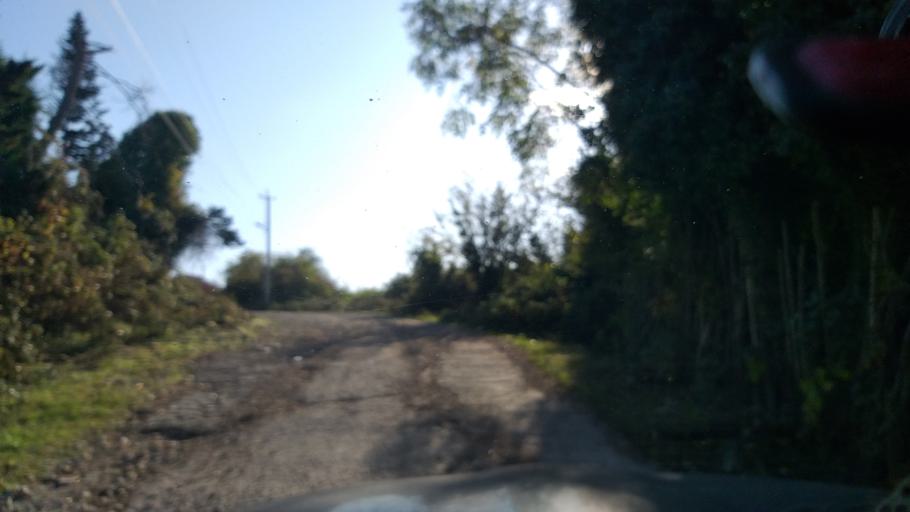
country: GE
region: Abkhazia
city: Stantsiya Novyy Afon
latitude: 43.0649
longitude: 40.8829
